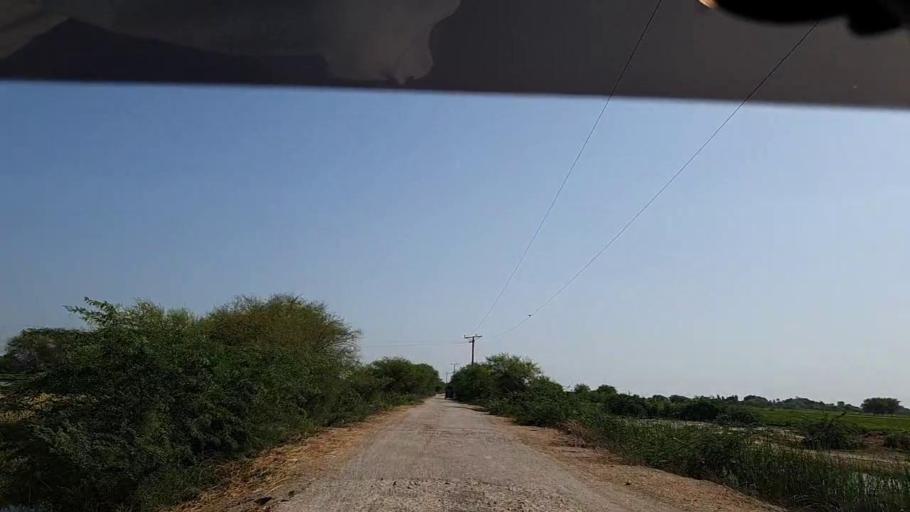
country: PK
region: Sindh
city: Badin
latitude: 24.6482
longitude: 68.7876
